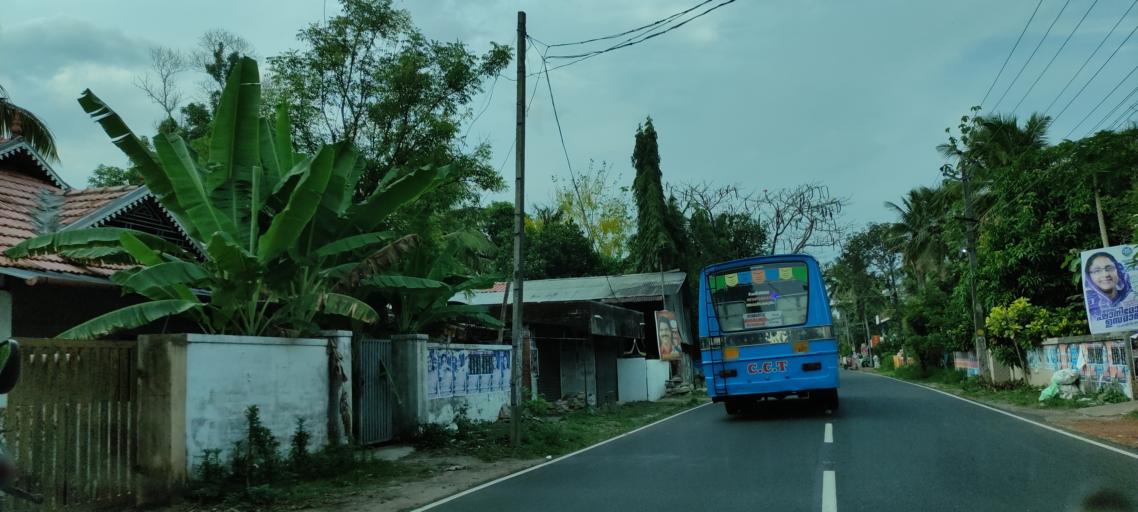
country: IN
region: Kerala
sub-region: Alappuzha
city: Kutiatodu
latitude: 9.7865
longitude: 76.3594
